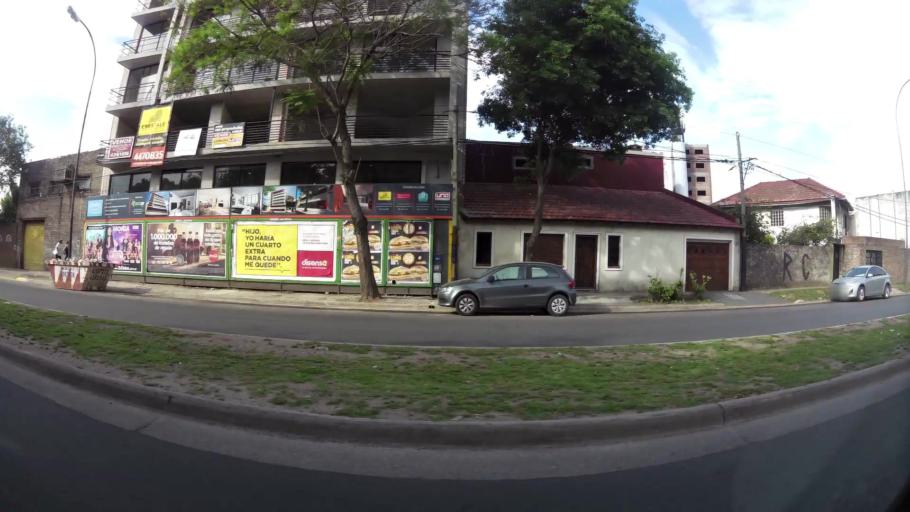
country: AR
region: Santa Fe
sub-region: Departamento de Rosario
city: Rosario
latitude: -32.9293
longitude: -60.6759
